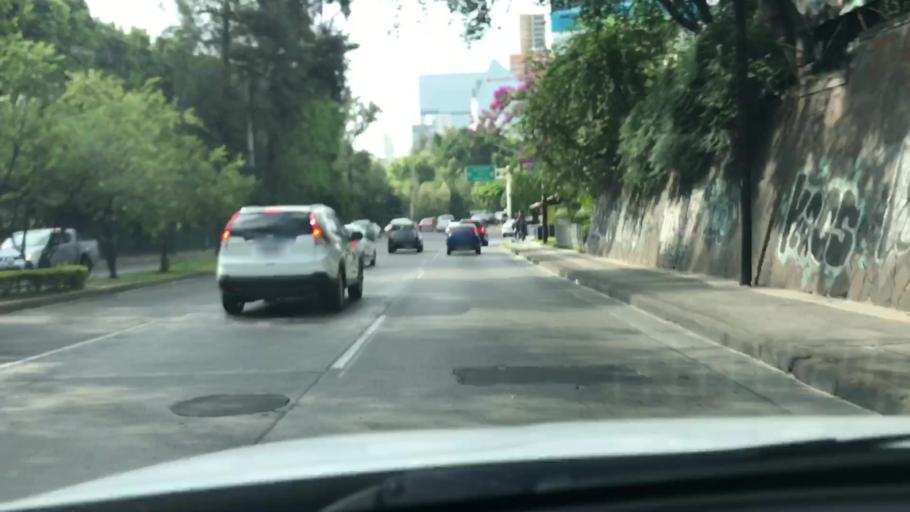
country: MX
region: Jalisco
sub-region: Zapopan
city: Zapopan
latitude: 20.7070
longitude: -103.3774
